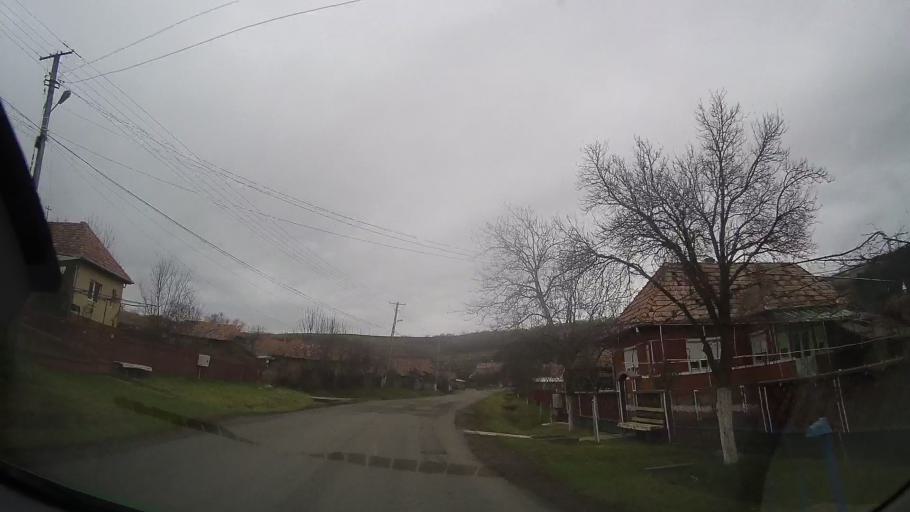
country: RO
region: Mures
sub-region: Comuna Bala
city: Bala
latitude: 46.7130
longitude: 24.5010
